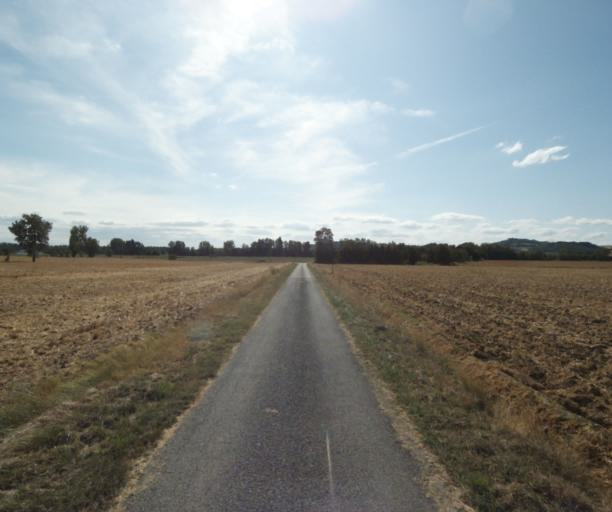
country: FR
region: Midi-Pyrenees
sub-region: Departement de la Haute-Garonne
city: Revel
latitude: 43.5059
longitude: 1.9715
